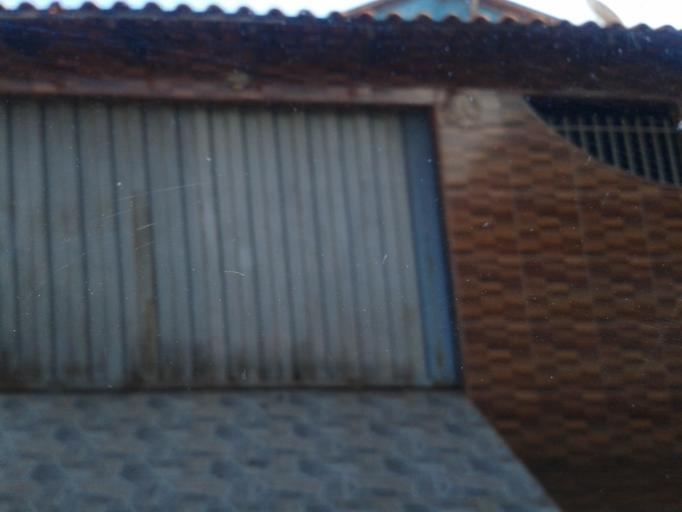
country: BR
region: Minas Gerais
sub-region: Capinopolis
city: Capinopolis
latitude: -18.5110
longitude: -49.5029
